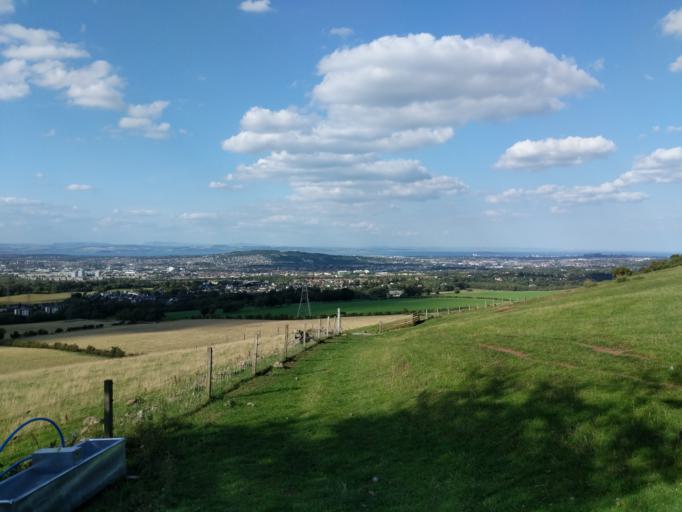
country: GB
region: Scotland
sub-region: Edinburgh
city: Currie
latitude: 55.8922
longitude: -3.2883
